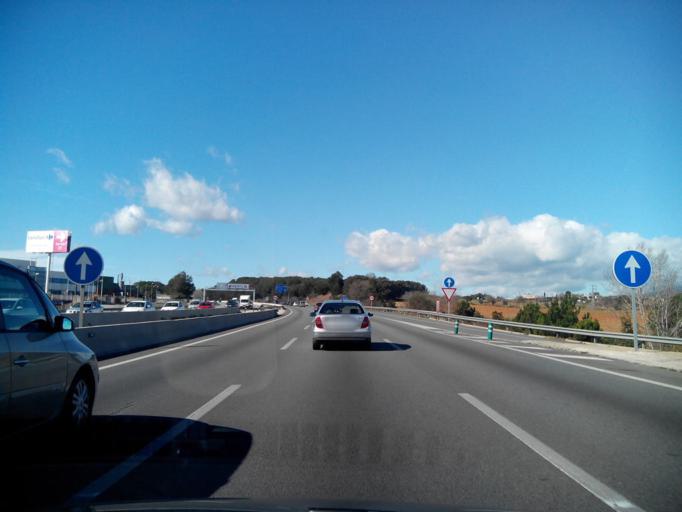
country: ES
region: Catalonia
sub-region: Provincia de Barcelona
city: Sant Quirze del Valles
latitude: 41.5423
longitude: 2.0797
